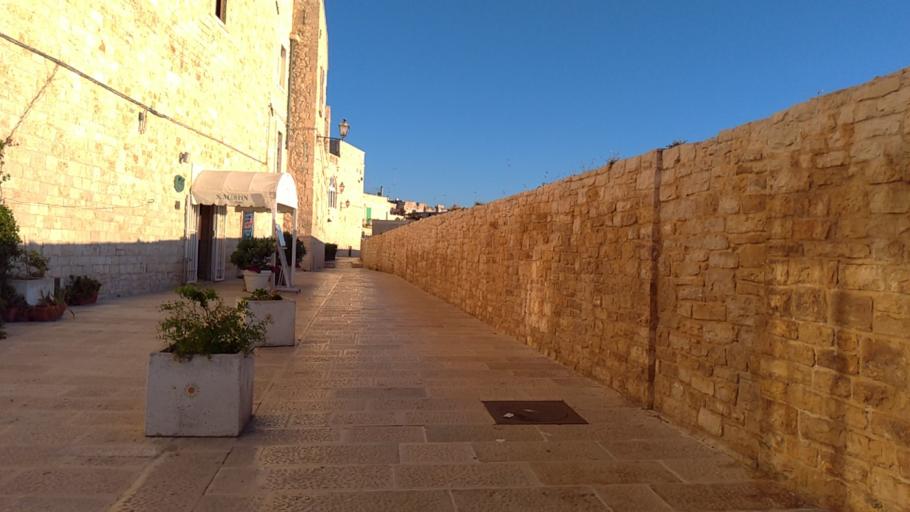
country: IT
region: Apulia
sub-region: Provincia di Bari
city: Giovinazzo
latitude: 41.1884
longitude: 16.6753
